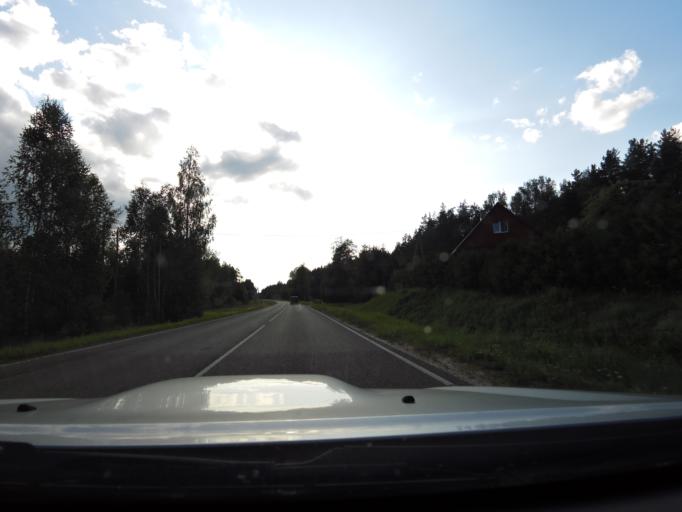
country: LT
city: Juodupe
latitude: 56.2062
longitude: 25.5998
